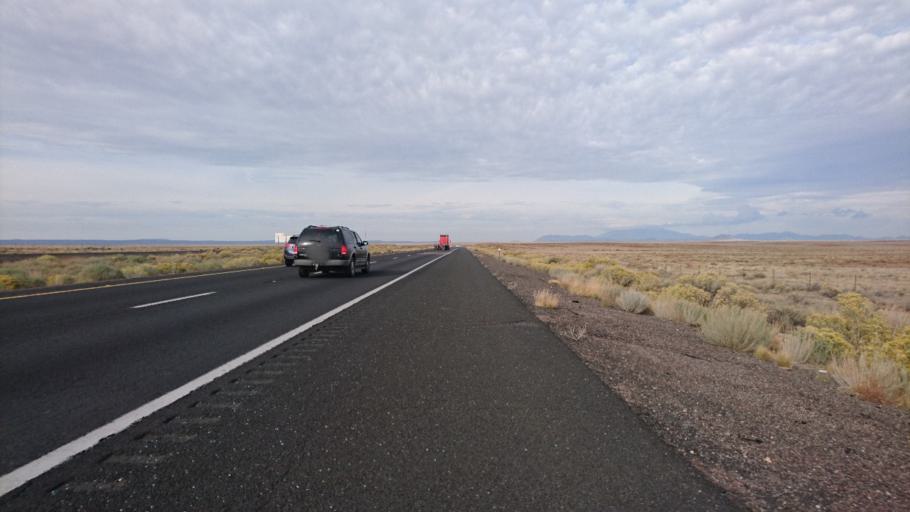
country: US
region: Arizona
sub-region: Coconino County
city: LeChee
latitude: 35.1126
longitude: -111.0516
